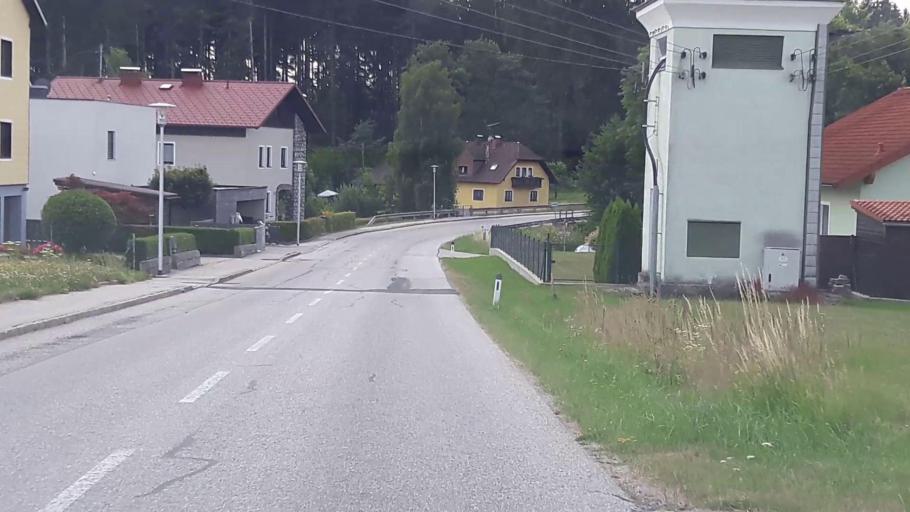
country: AT
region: Upper Austria
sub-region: Politischer Bezirk Rohrbach
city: Kleinzell im Muehlkreis
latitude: 48.4821
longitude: 13.9647
